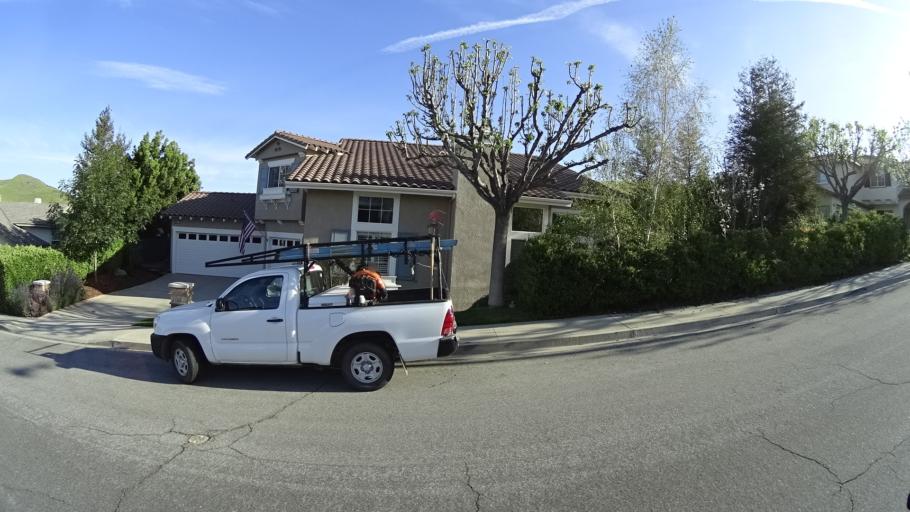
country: US
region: California
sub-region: Ventura County
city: Thousand Oaks
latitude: 34.2166
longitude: -118.8122
